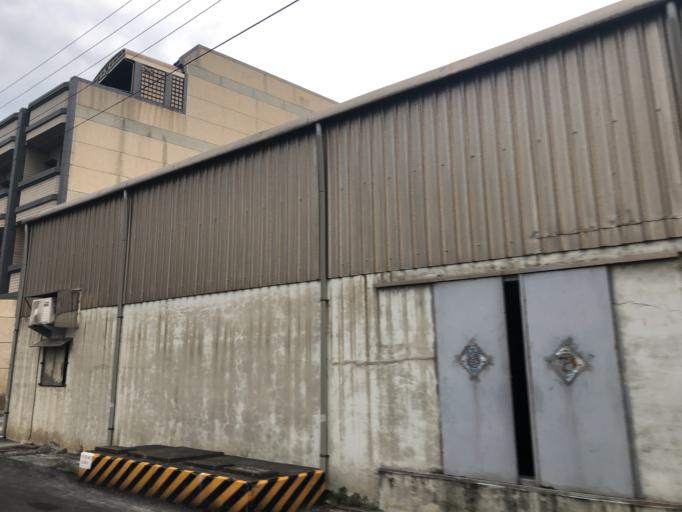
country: TW
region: Taiwan
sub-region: Chiayi
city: Taibao
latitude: 23.7102
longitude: 120.2008
